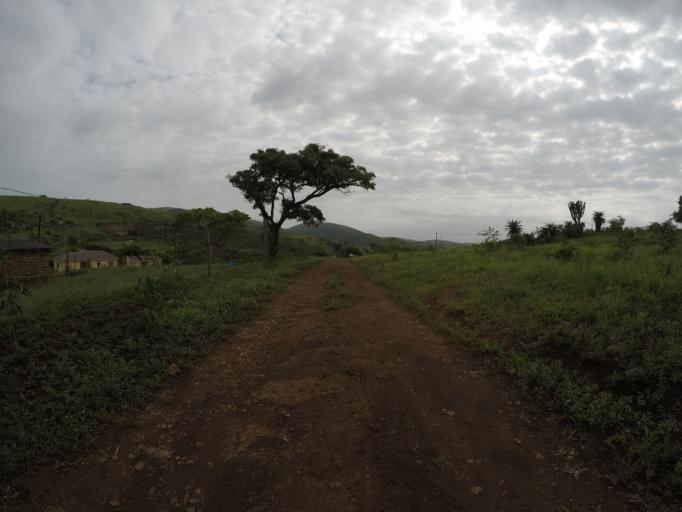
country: ZA
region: KwaZulu-Natal
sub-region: uThungulu District Municipality
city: Empangeni
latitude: -28.6296
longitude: 31.9062
